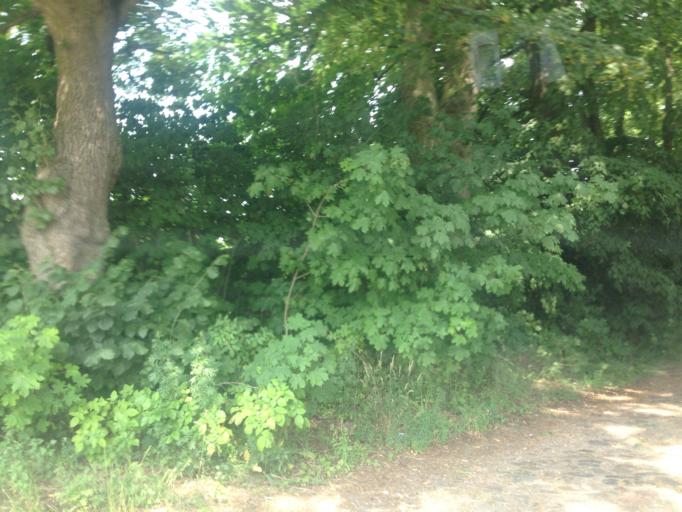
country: PL
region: Kujawsko-Pomorskie
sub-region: Powiat brodnicki
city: Bobrowo
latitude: 53.2434
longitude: 19.2590
